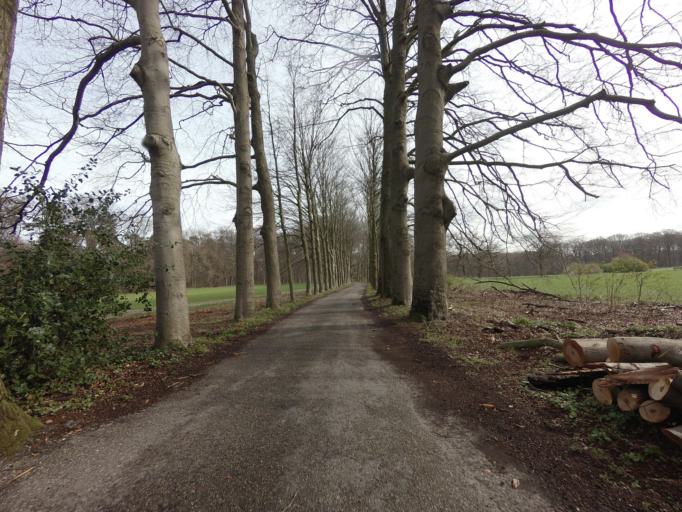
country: NL
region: Gelderland
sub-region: Gemeente Arnhem
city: Hoogkamp
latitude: 52.0047
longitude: 5.8617
